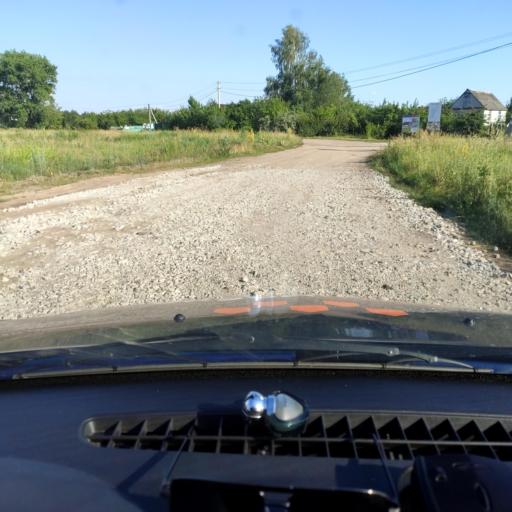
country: RU
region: Voronezj
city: Podgornoye
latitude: 51.8656
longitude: 39.1739
